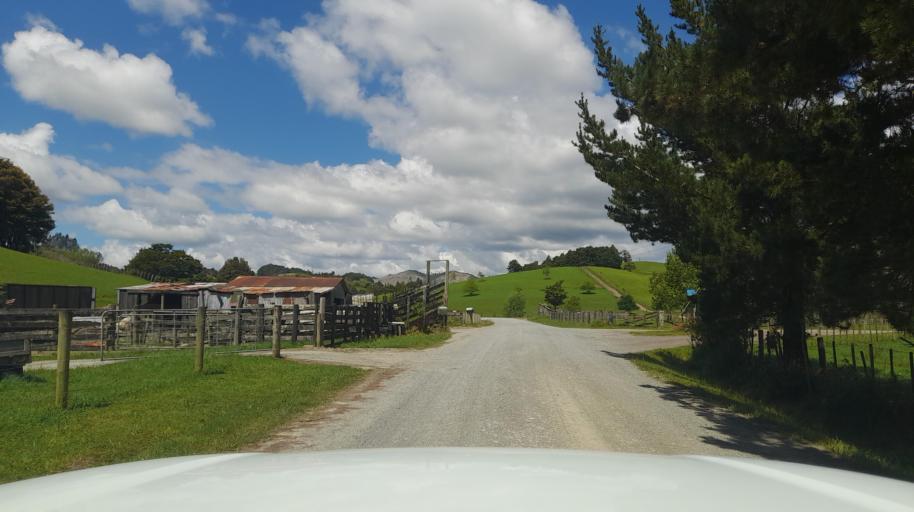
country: NZ
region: Northland
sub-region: Far North District
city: Kaitaia
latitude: -35.1209
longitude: 173.3994
